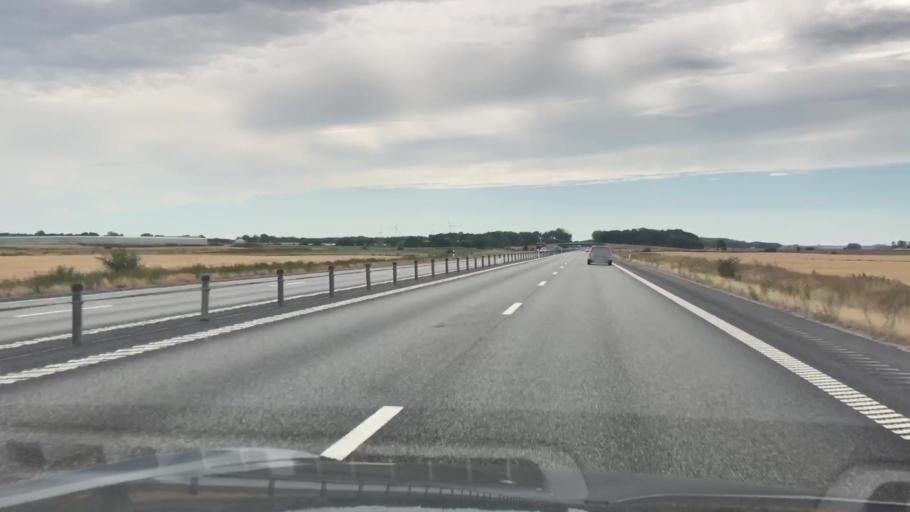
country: SE
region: Blekinge
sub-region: Karlshamns Kommun
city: Morrum
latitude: 56.1266
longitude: 14.6600
